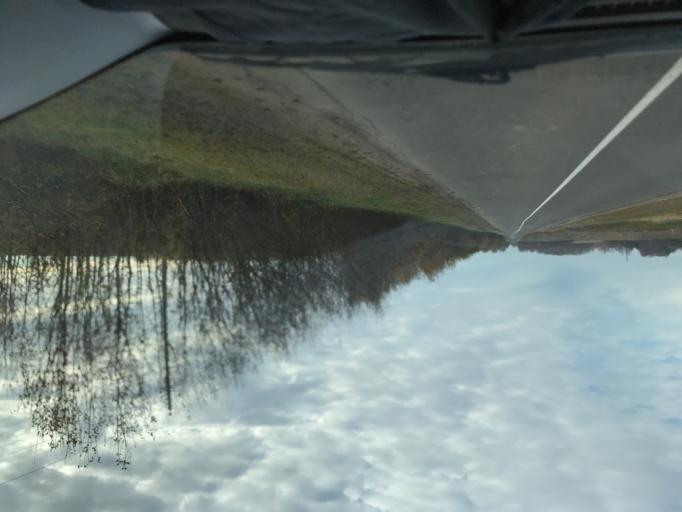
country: BY
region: Vitebsk
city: Haradok
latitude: 55.4111
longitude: 29.7561
